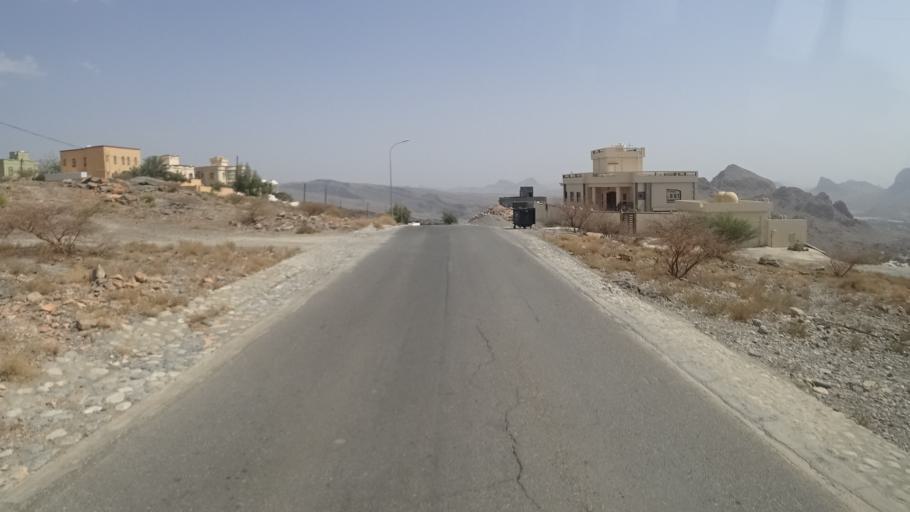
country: OM
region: Muhafazat ad Dakhiliyah
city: Bahla'
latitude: 23.1349
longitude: 57.3042
